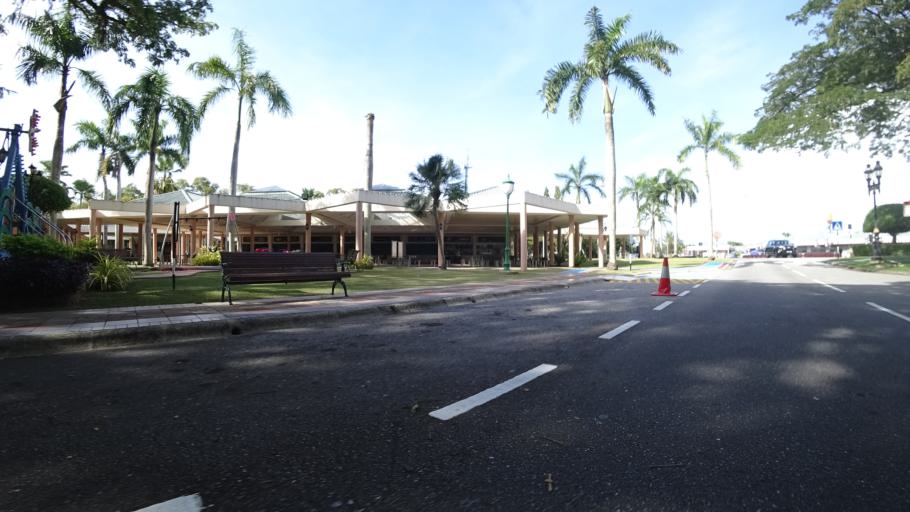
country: BN
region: Brunei and Muara
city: Bandar Seri Begawan
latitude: 4.9364
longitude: 114.8327
